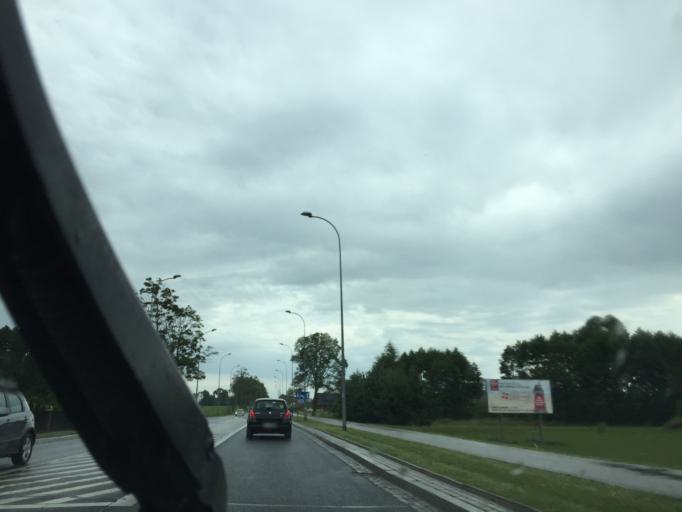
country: PL
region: Podlasie
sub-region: Bialystok
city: Bialystok
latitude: 53.0939
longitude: 23.2381
